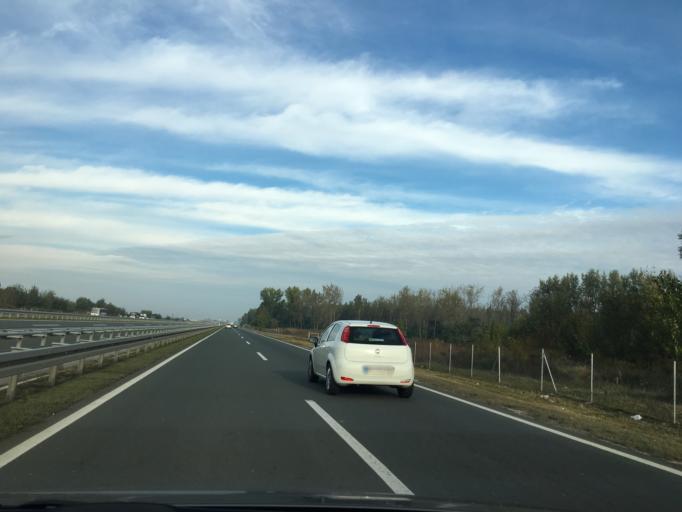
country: RS
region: Autonomna Pokrajina Vojvodina
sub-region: Juznobacki Okrug
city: Petrovaradin
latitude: 45.2925
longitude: 19.8831
